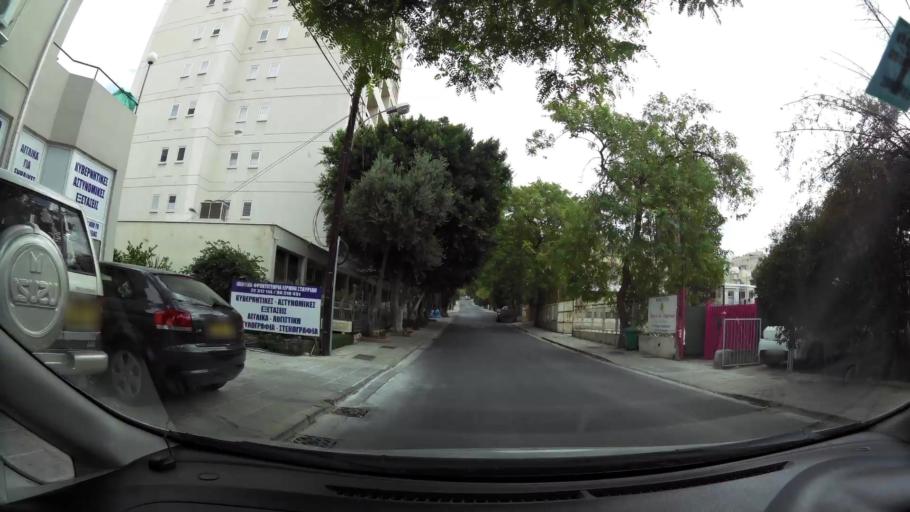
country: CY
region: Lefkosia
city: Nicosia
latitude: 35.1593
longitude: 33.3595
